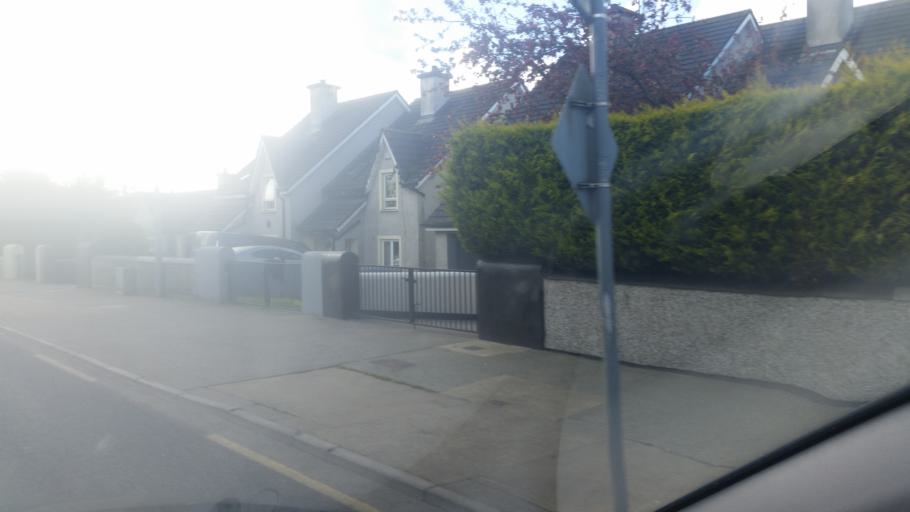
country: IE
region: Leinster
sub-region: Loch Garman
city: Enniscorthy
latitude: 52.4990
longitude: -6.5520
